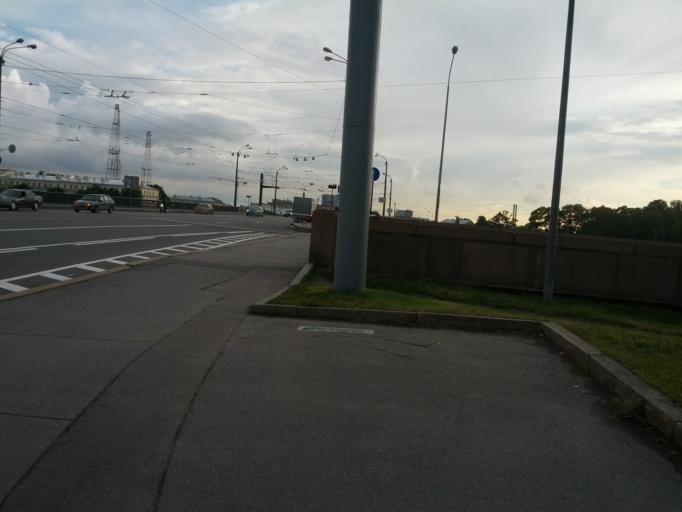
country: RU
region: Leningrad
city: Sampsonievskiy
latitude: 59.9686
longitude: 30.3370
